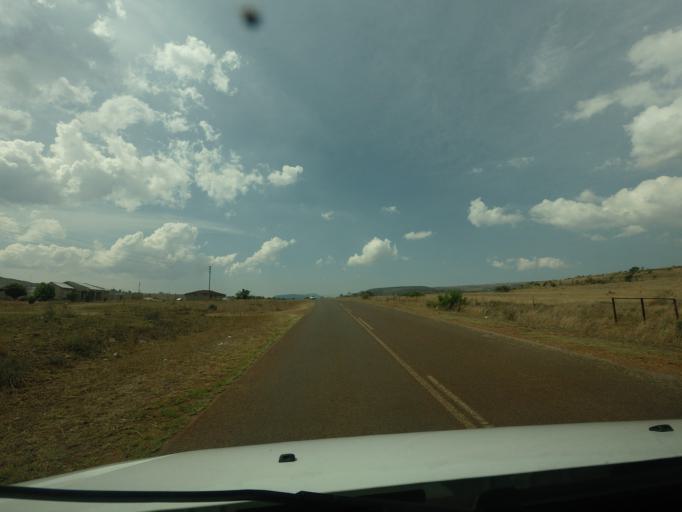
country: ZA
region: Mpumalanga
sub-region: Ehlanzeni District
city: Graksop
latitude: -24.6571
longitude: 30.8184
